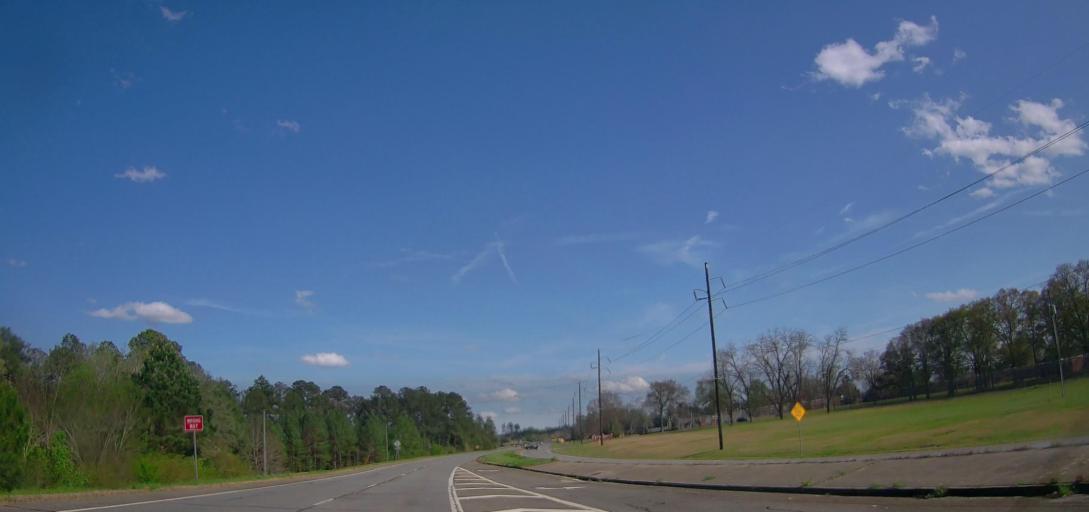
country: US
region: Georgia
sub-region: Baldwin County
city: Milledgeville
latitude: 33.0935
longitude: -83.2544
